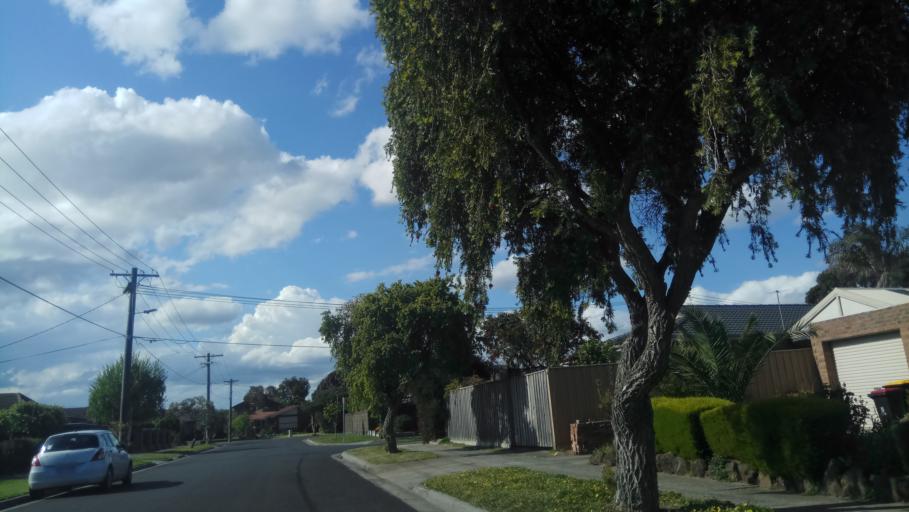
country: AU
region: Victoria
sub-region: Kingston
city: Dingley Village
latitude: -37.9848
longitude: 145.1247
